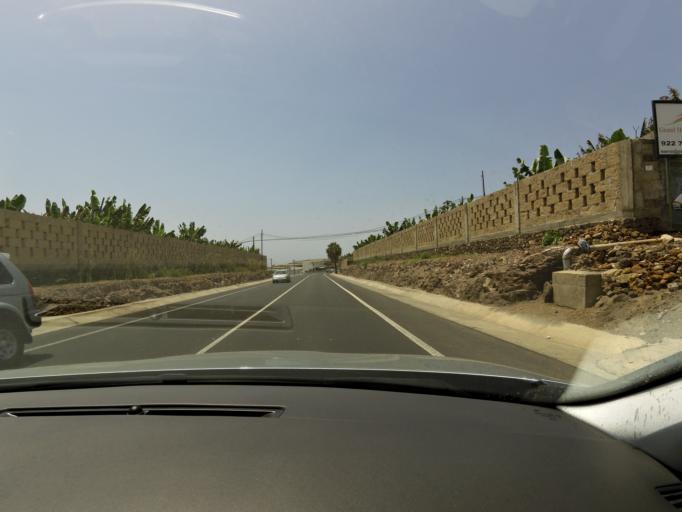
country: ES
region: Canary Islands
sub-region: Provincia de Santa Cruz de Tenerife
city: Adeje
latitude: 28.1305
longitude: -16.7619
